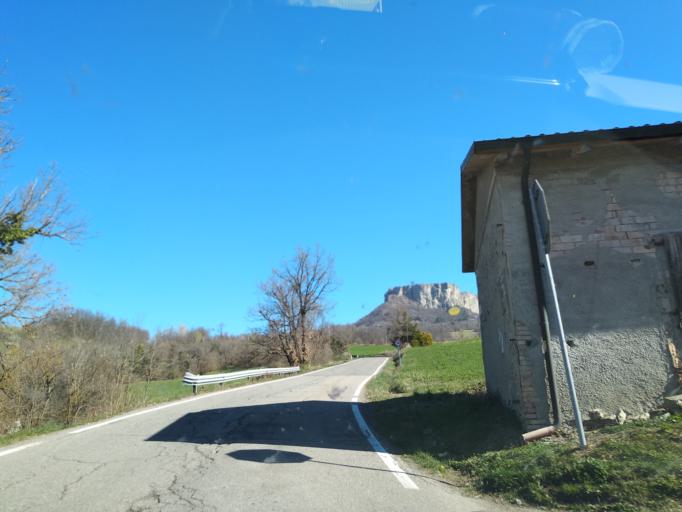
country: IT
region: Emilia-Romagna
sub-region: Provincia di Reggio Emilia
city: Castelnovo ne'Monti
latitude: 44.4044
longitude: 10.3986
